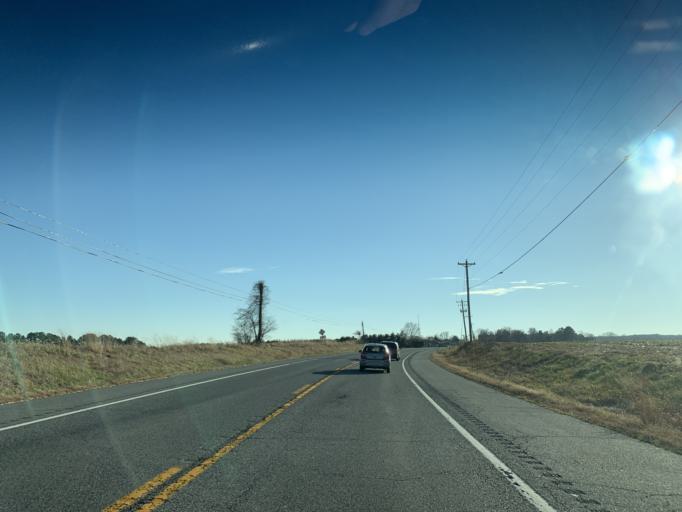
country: US
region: Delaware
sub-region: New Castle County
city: Middletown
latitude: 39.4166
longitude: -75.8614
